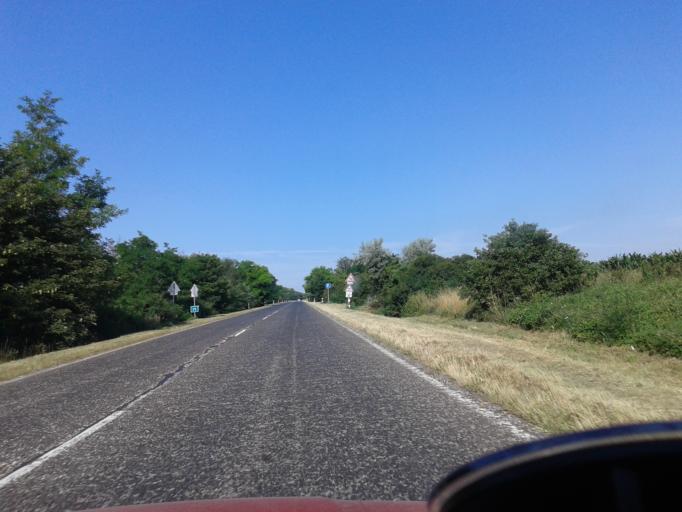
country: HU
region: Pest
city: Zsambek
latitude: 47.4959
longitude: 18.7121
